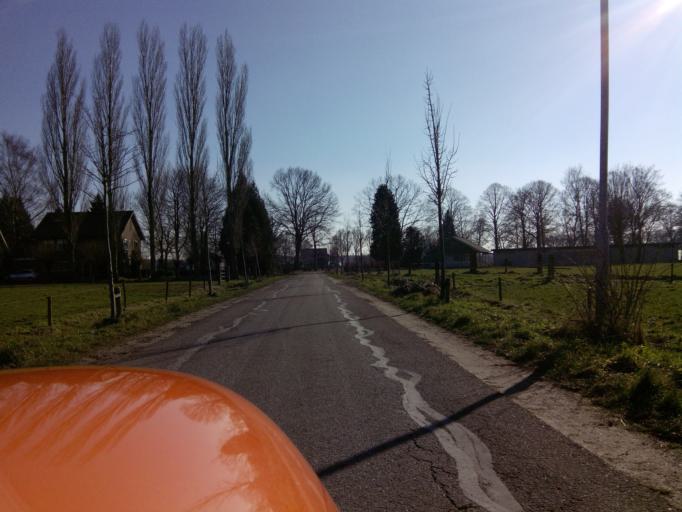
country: NL
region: Gelderland
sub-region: Gemeente Barneveld
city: Terschuur
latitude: 52.1152
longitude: 5.5113
